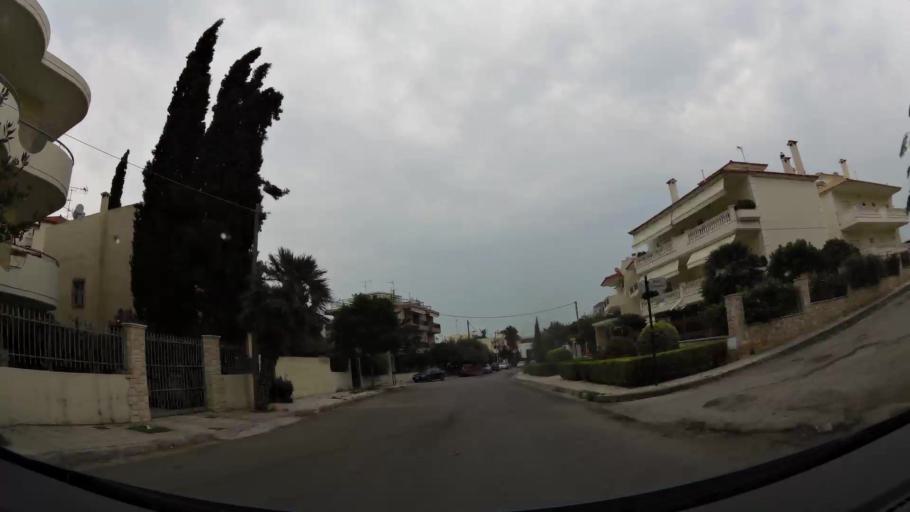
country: GR
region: Attica
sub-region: Nomarchia Athinas
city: Alimos
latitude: 37.9107
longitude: 23.7323
